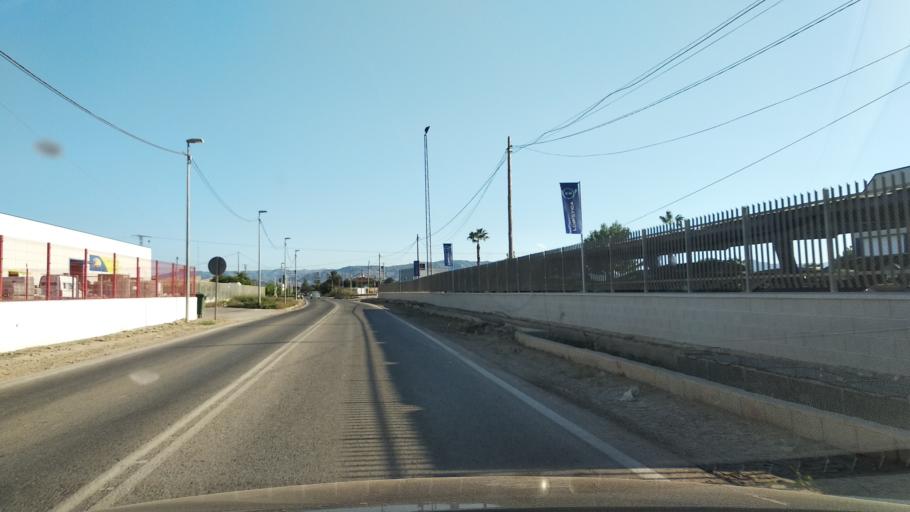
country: ES
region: Murcia
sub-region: Murcia
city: Santomera
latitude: 38.0503
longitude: -1.0558
